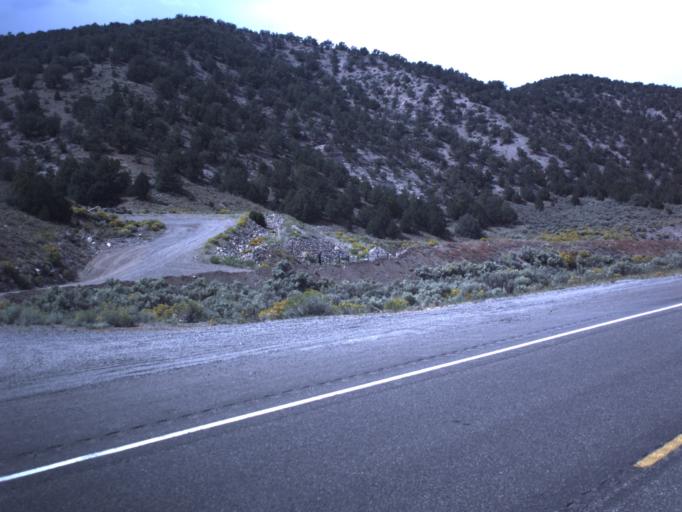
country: US
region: Utah
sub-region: Garfield County
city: Panguitch
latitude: 37.7703
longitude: -112.3911
